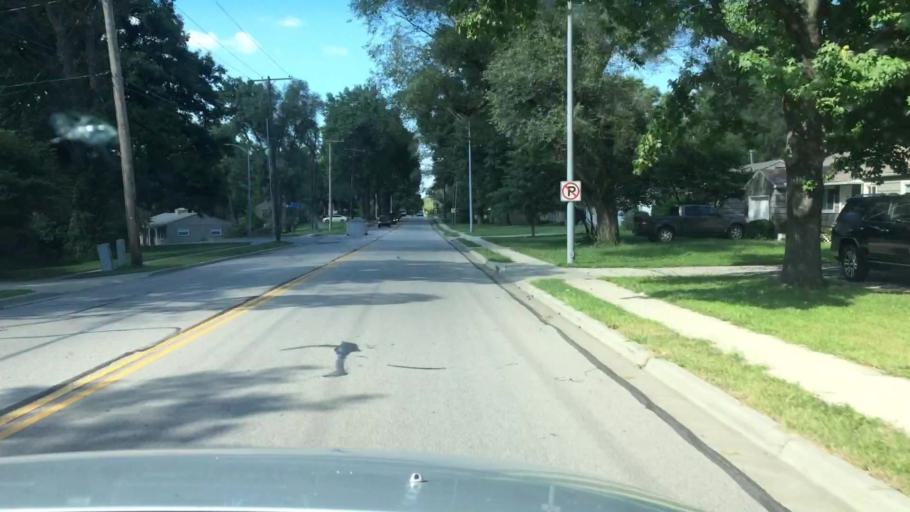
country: US
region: Kansas
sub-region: Johnson County
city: Prairie Village
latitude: 38.9878
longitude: -94.6490
